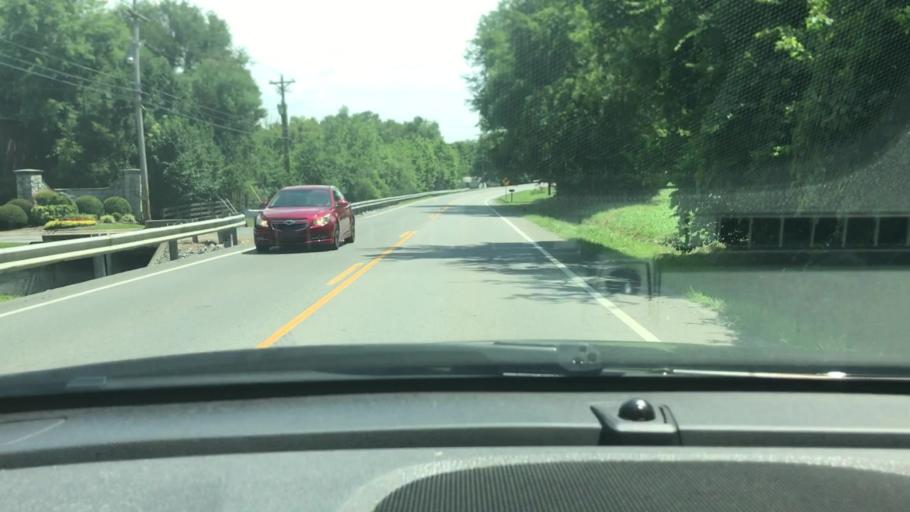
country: US
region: Tennessee
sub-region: Sumner County
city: Shackle Island
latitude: 36.3421
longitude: -86.6139
